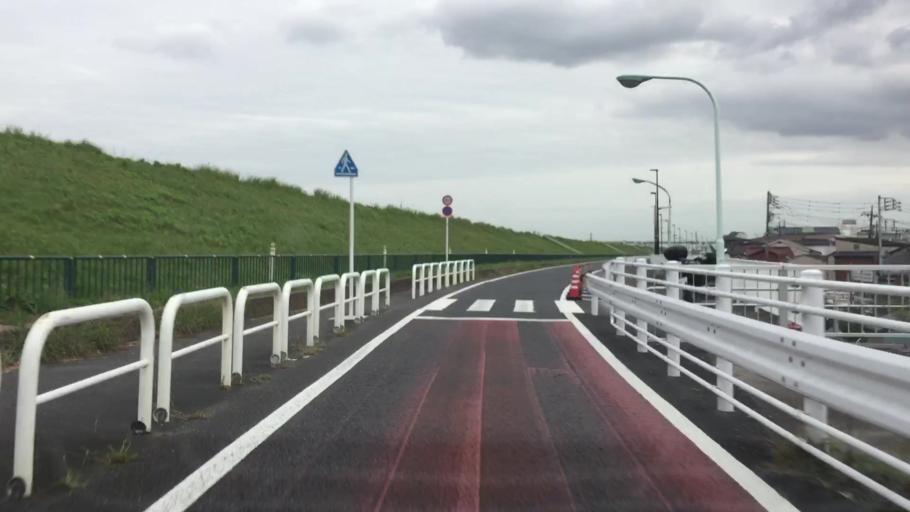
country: JP
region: Saitama
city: Soka
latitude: 35.7534
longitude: 139.8100
